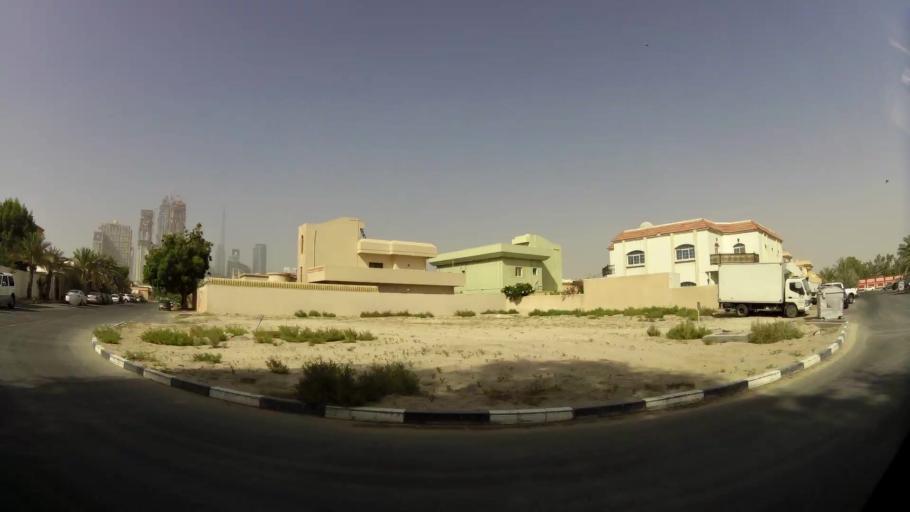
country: AE
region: Dubai
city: Dubai
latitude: 25.1750
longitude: 55.2489
